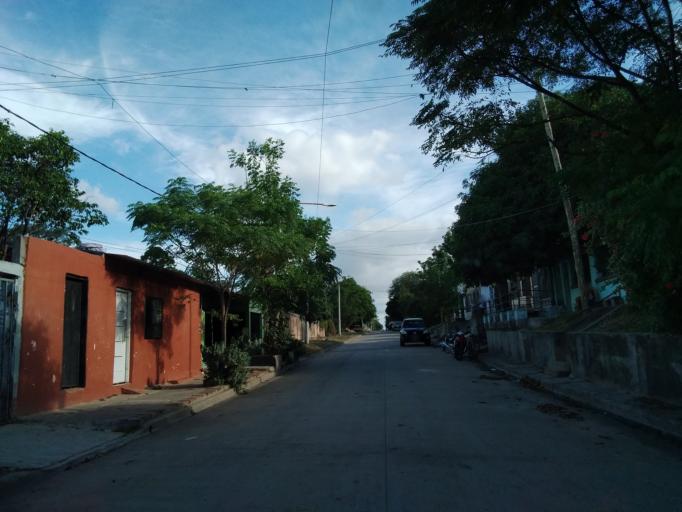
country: AR
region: Corrientes
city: Corrientes
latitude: -27.4623
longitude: -58.8121
